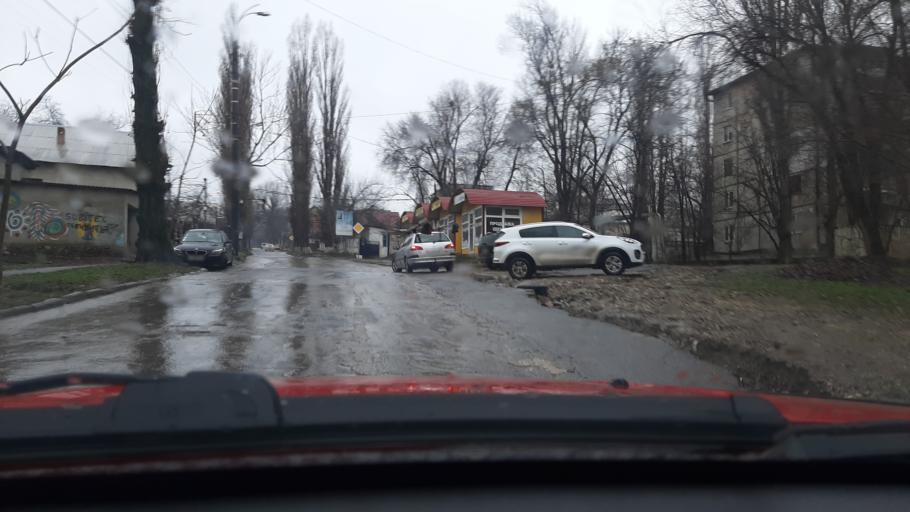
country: MD
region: Chisinau
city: Chisinau
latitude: 47.0016
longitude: 28.8696
